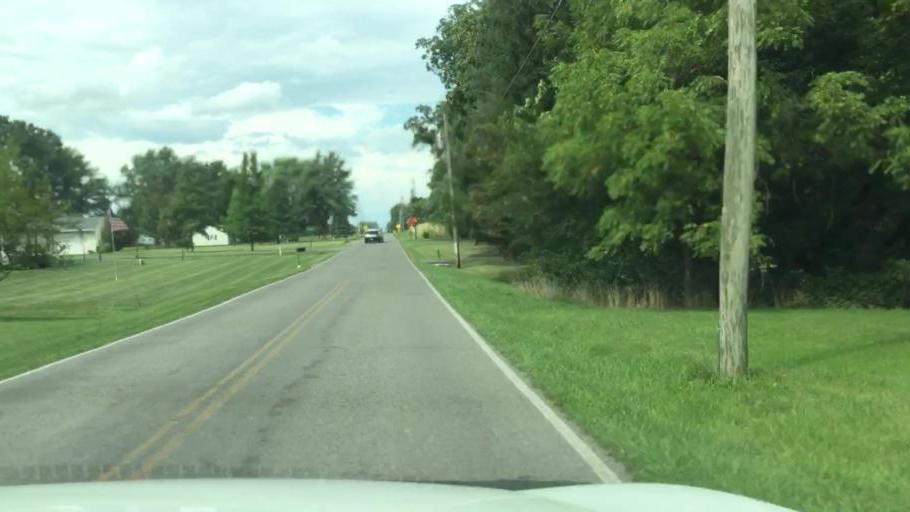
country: US
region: Ohio
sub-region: Champaign County
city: Urbana
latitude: 40.0951
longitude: -83.7137
